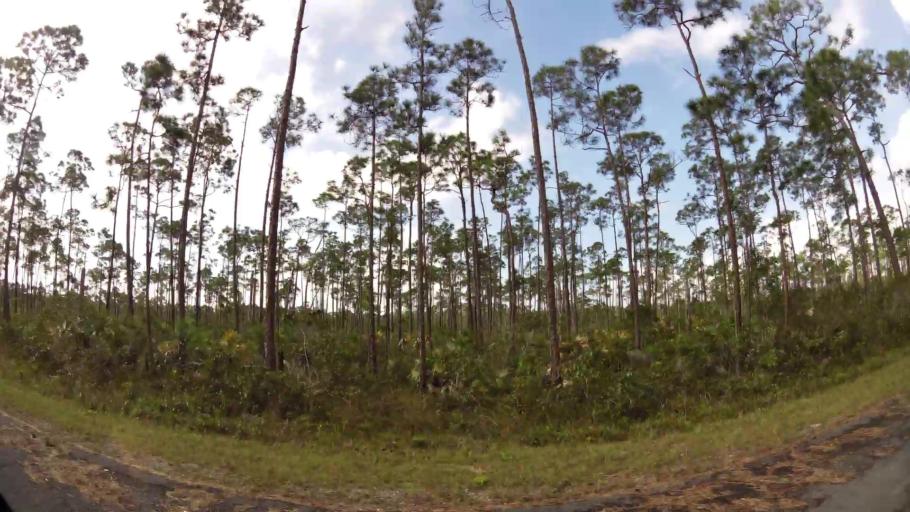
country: BS
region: Freeport
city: Lucaya
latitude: 26.5839
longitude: -78.5499
